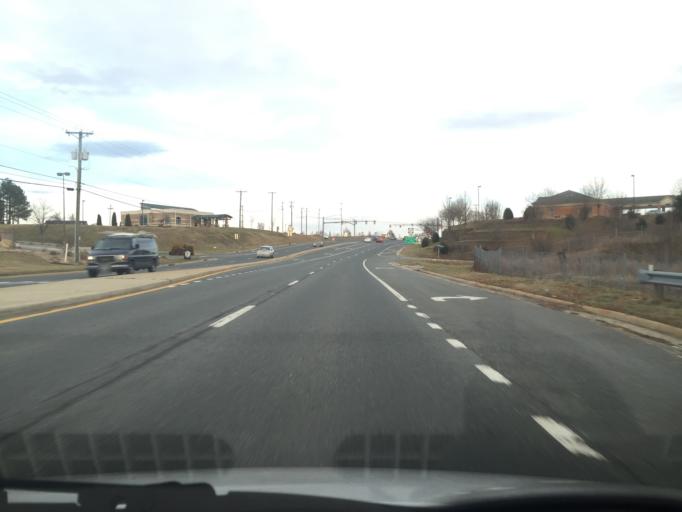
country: US
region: Virginia
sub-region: Bedford County
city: Forest
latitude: 37.3708
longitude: -79.3049
